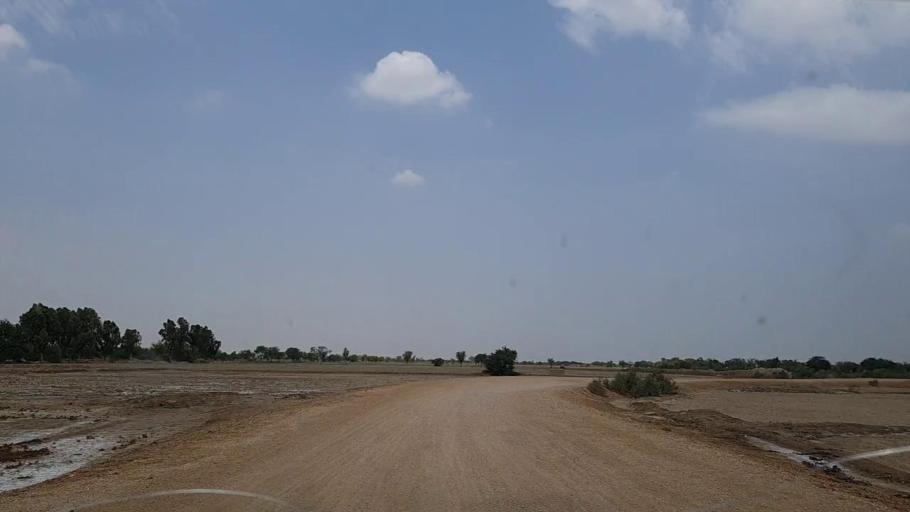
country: PK
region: Sindh
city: Phulji
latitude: 26.8190
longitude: 67.6339
